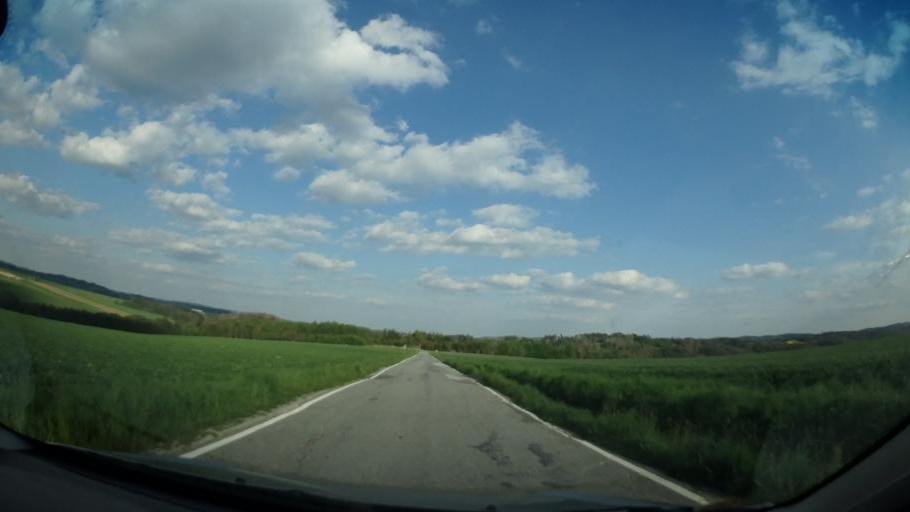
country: CZ
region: Vysocina
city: Merin
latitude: 49.3483
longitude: 15.9056
